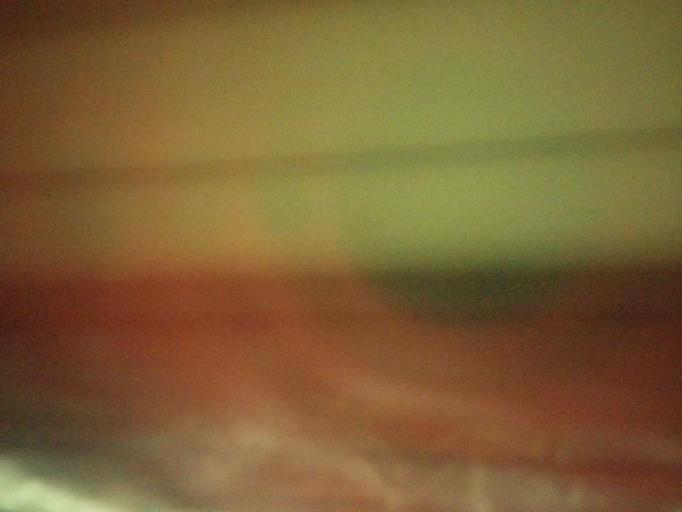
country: JP
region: Shizuoka
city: Yaizu
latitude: 34.9174
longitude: 138.3557
